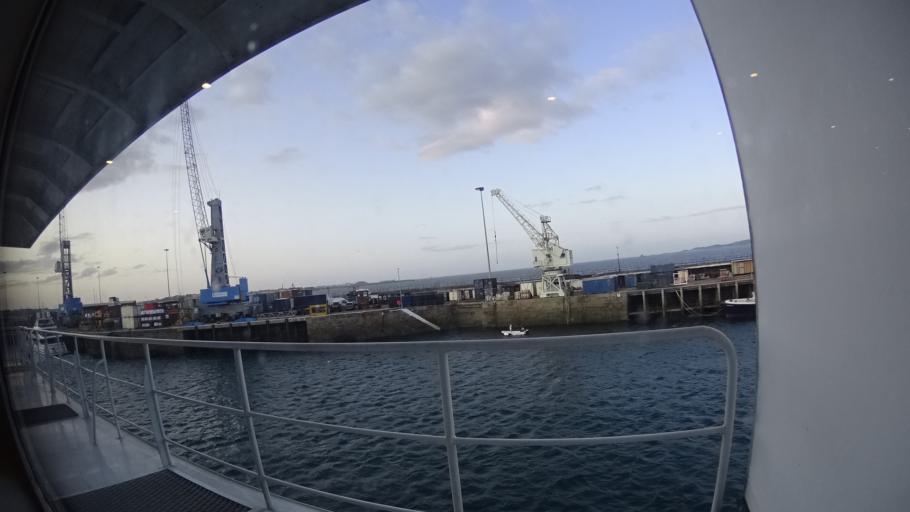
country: GG
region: St Peter Port
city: Saint Peter Port
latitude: 49.4568
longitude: -2.5277
